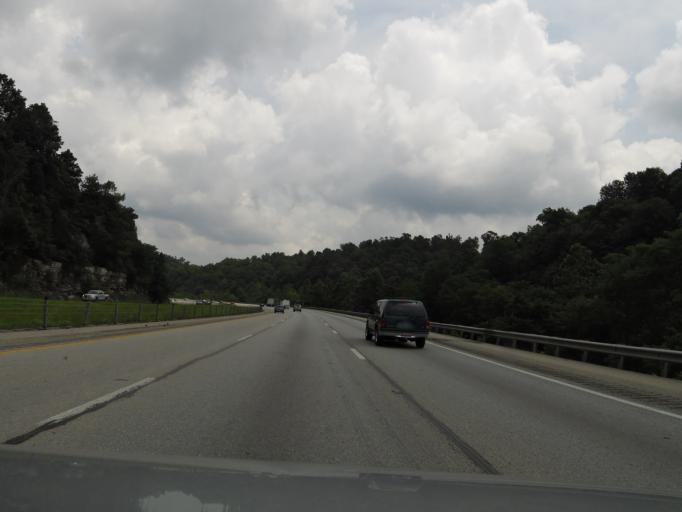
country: US
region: Kentucky
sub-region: Hardin County
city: Elizabethtown
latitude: 37.7413
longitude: -85.7976
